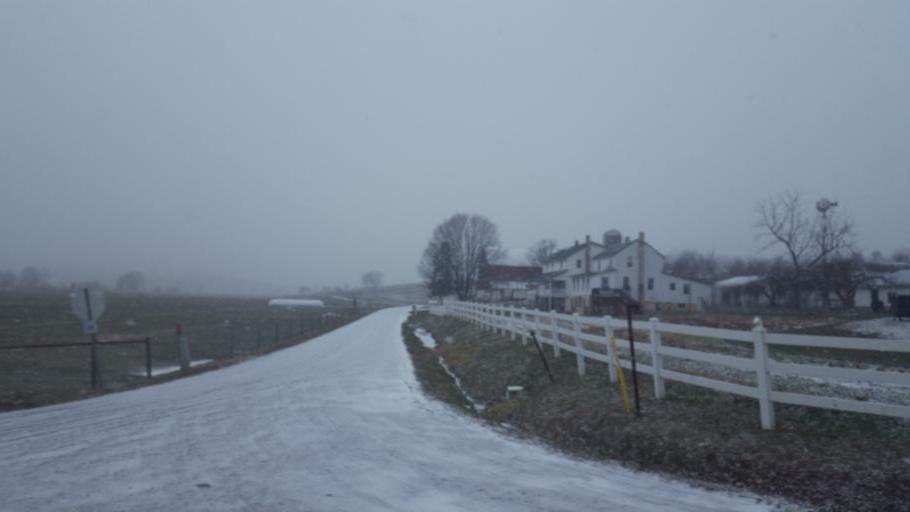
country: US
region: Ohio
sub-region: Tuscarawas County
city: Sugarcreek
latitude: 40.4696
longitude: -81.7275
